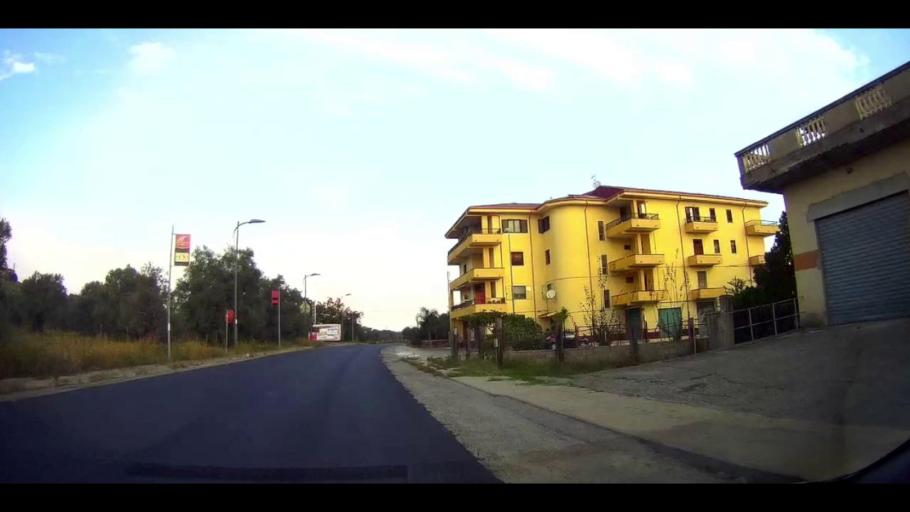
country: IT
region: Calabria
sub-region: Provincia di Crotone
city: Torretta
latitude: 39.4600
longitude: 17.0296
